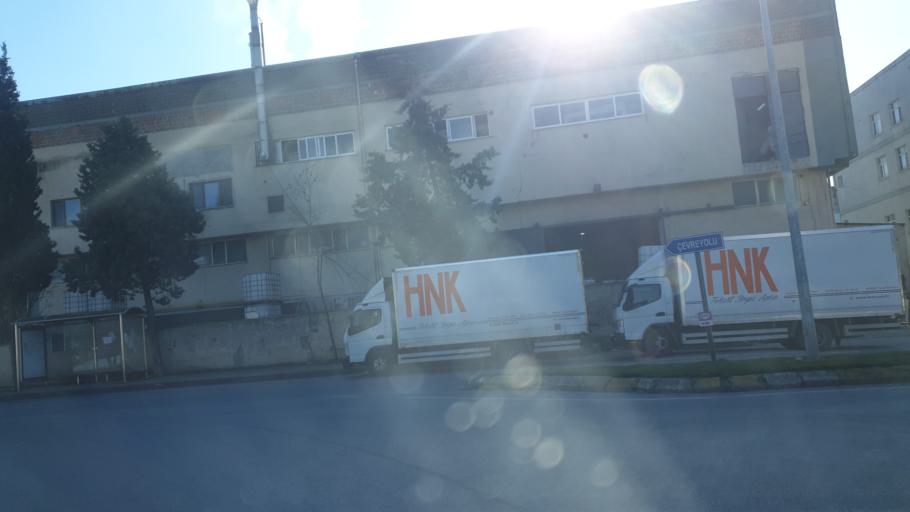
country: TR
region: Kocaeli
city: Balcik
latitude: 40.8810
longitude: 29.3707
